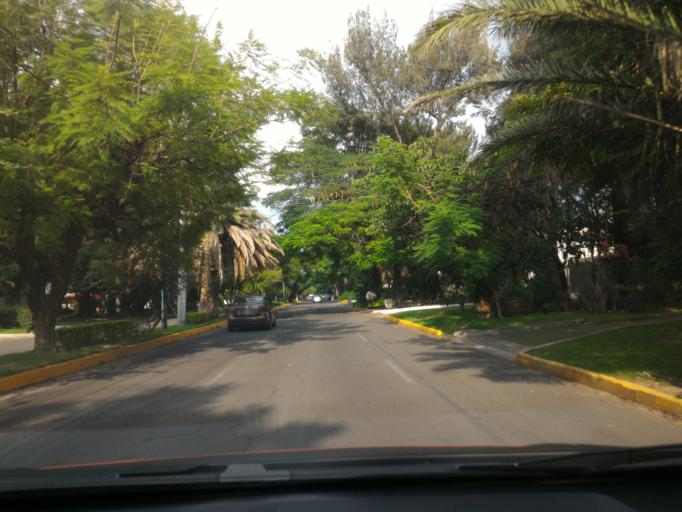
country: MX
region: Jalisco
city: Guadalajara
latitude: 20.6607
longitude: -103.3933
